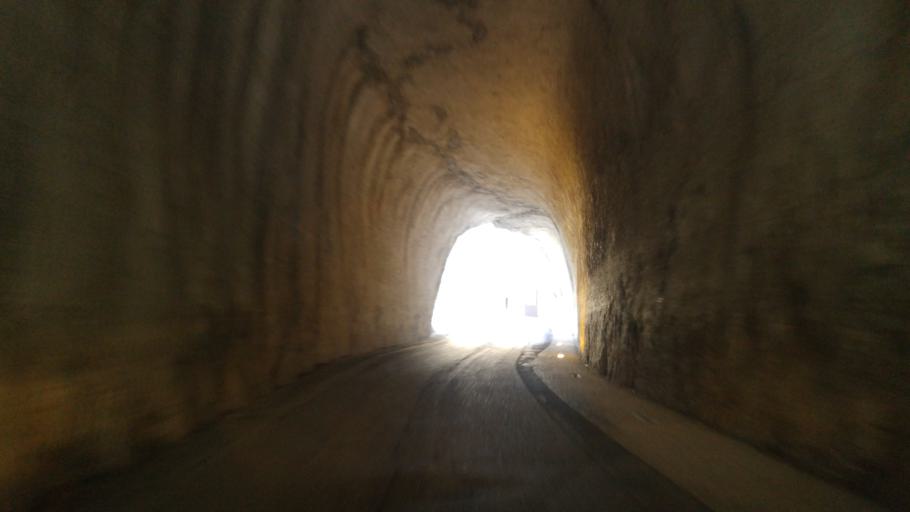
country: IT
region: The Marches
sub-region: Provincia di Pesaro e Urbino
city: Canavaccio
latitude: 43.6533
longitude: 12.7307
